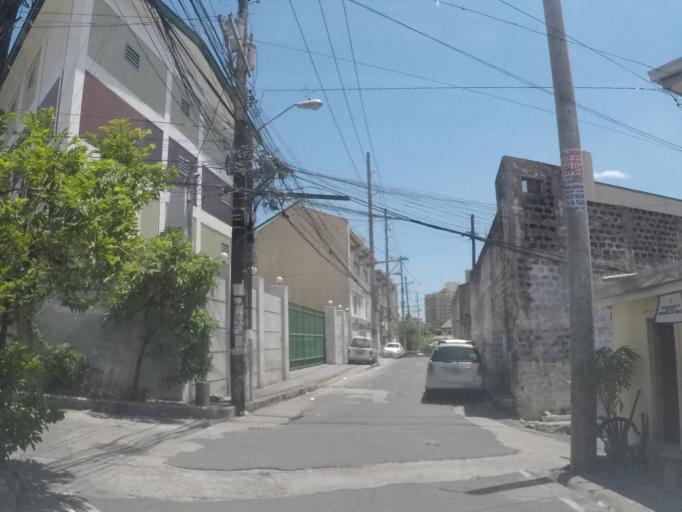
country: PH
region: Metro Manila
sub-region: San Juan
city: San Juan
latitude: 14.6024
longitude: 121.0236
